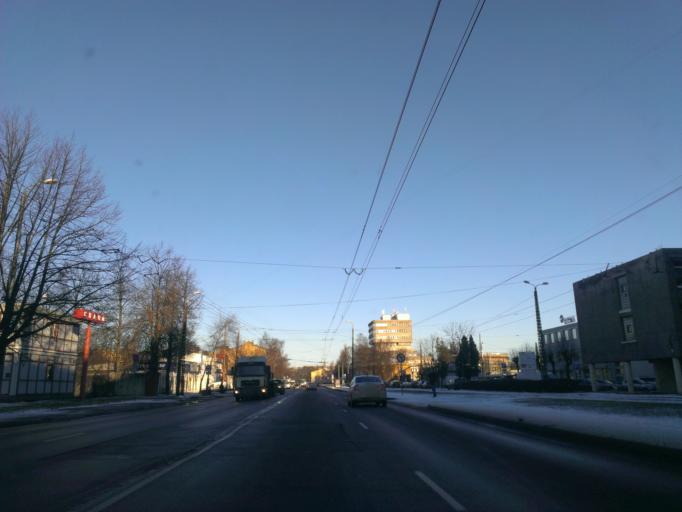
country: LV
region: Riga
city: Riga
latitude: 56.9864
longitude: 24.1211
